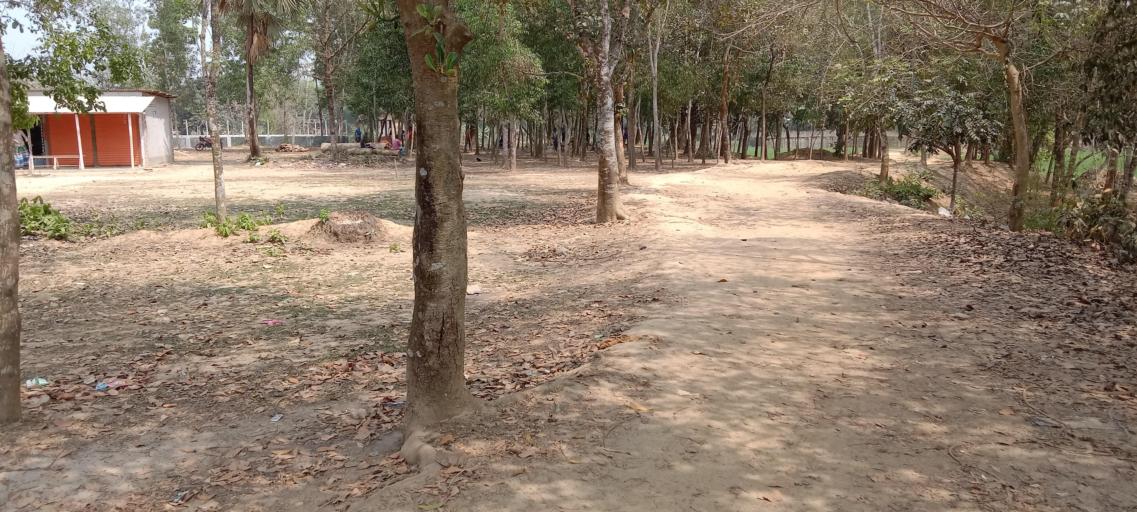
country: BD
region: Dhaka
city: Gafargaon
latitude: 24.4503
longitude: 90.3555
